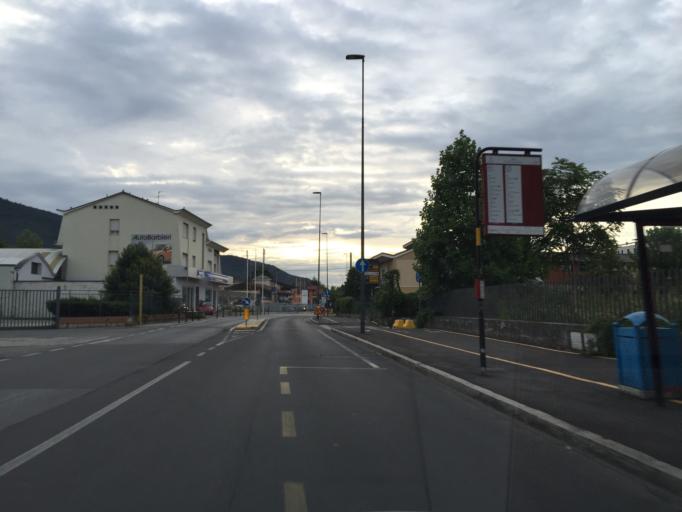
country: IT
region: Lombardy
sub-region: Provincia di Brescia
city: Brescia
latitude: 45.5279
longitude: 10.2366
